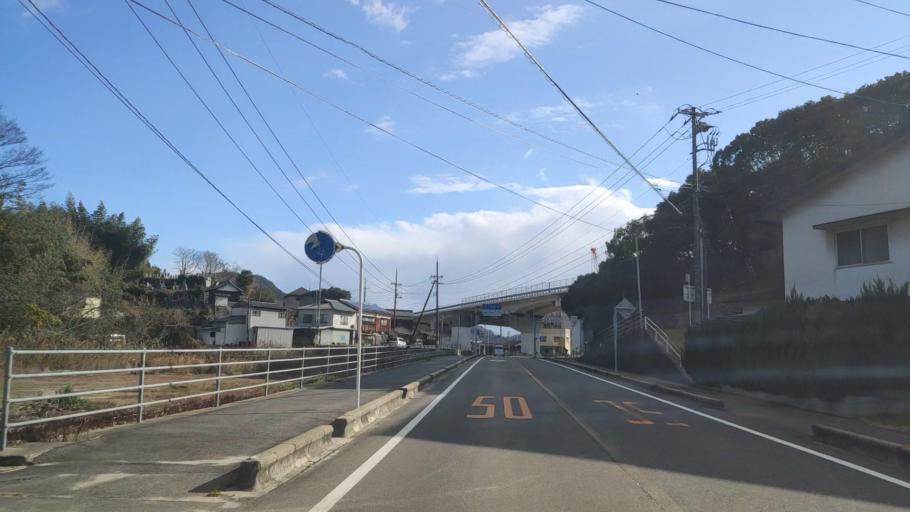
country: JP
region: Hiroshima
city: Innoshima
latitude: 34.2144
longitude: 133.0681
